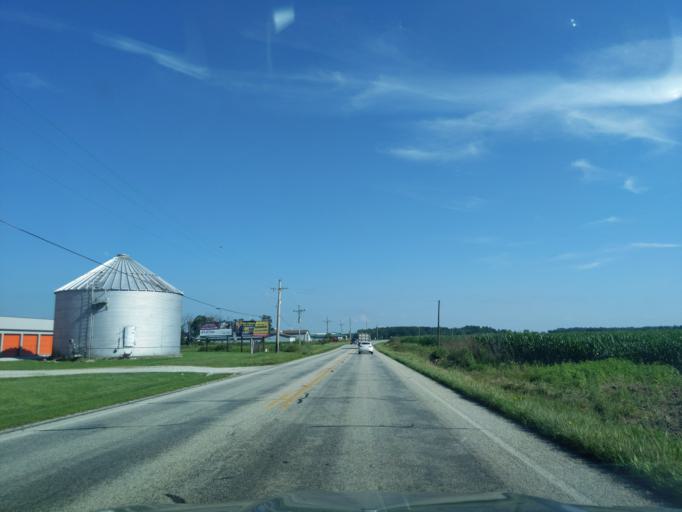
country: US
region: Indiana
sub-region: Ripley County
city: Osgood
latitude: 39.1172
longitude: -85.2821
